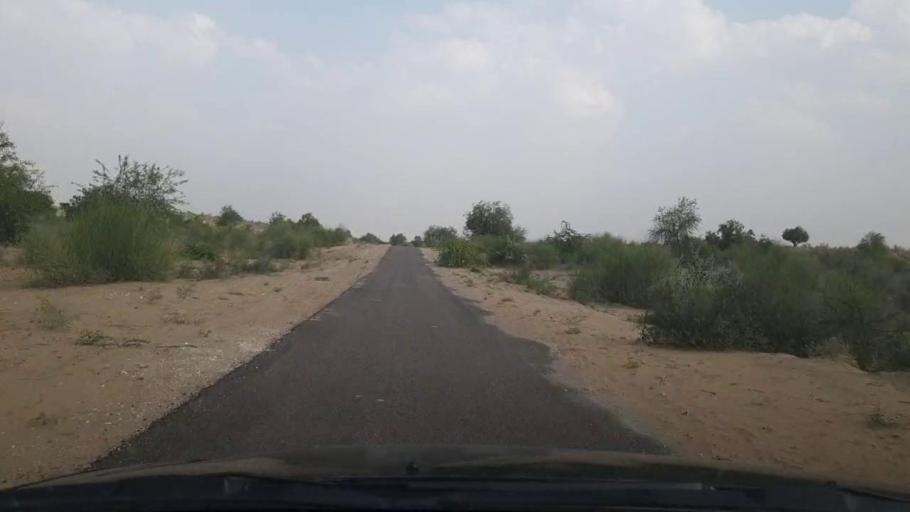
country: PK
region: Sindh
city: Islamkot
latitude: 25.0067
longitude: 70.6554
